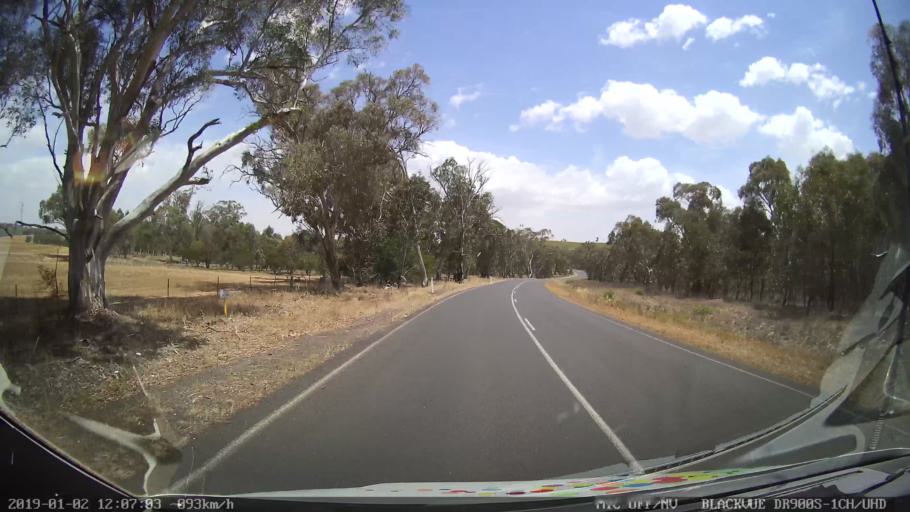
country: AU
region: New South Wales
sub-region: Young
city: Young
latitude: -34.4972
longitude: 148.2883
